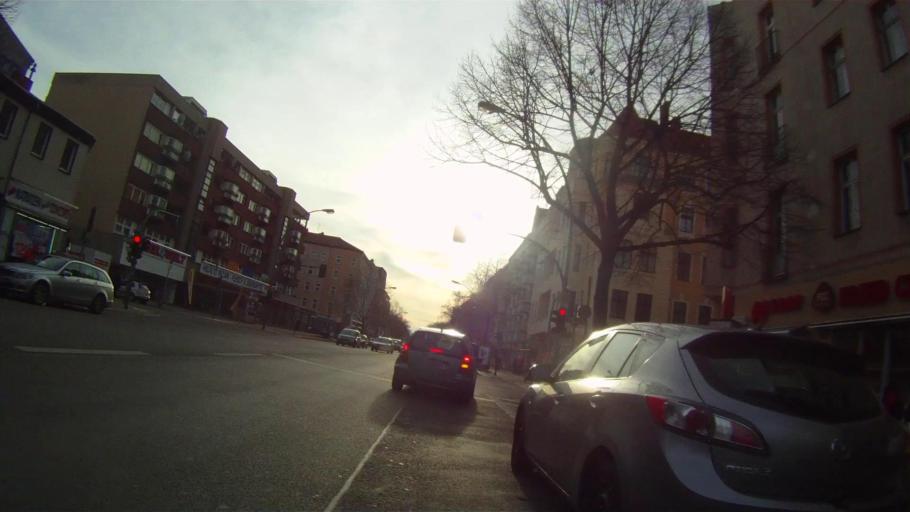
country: DE
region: Berlin
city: Berlin Treptow
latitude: 52.4763
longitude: 13.4269
